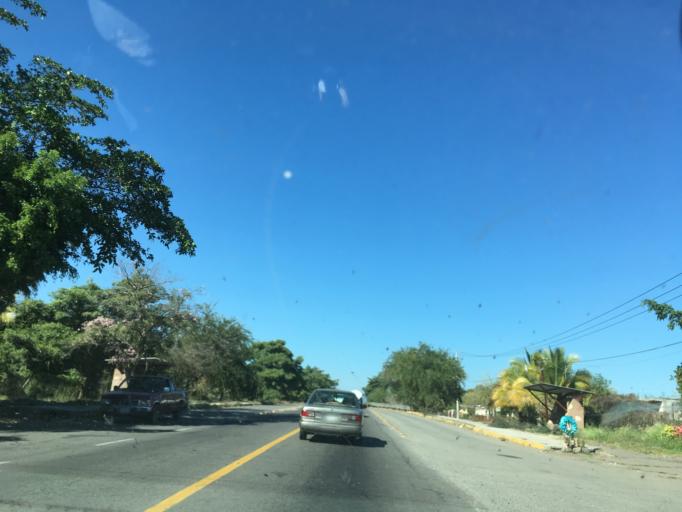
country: MX
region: Michoacan
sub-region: Gabriel Zamora
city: Lombardia
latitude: 19.0877
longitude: -102.0587
